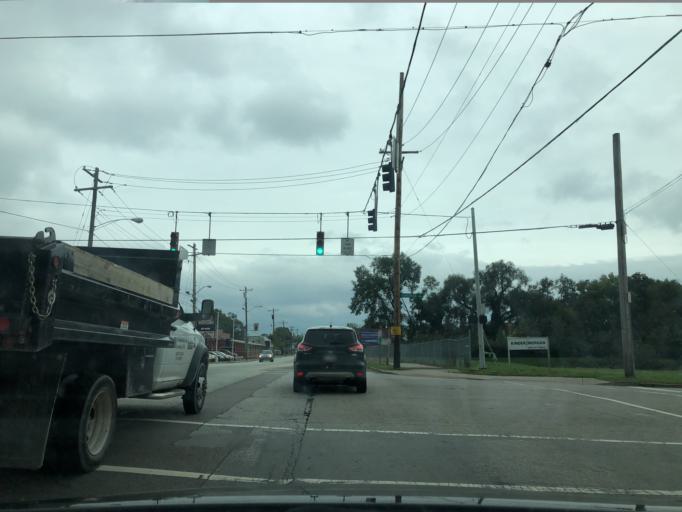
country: US
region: Kentucky
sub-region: Campbell County
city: Dayton
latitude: 39.1130
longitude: -84.4398
